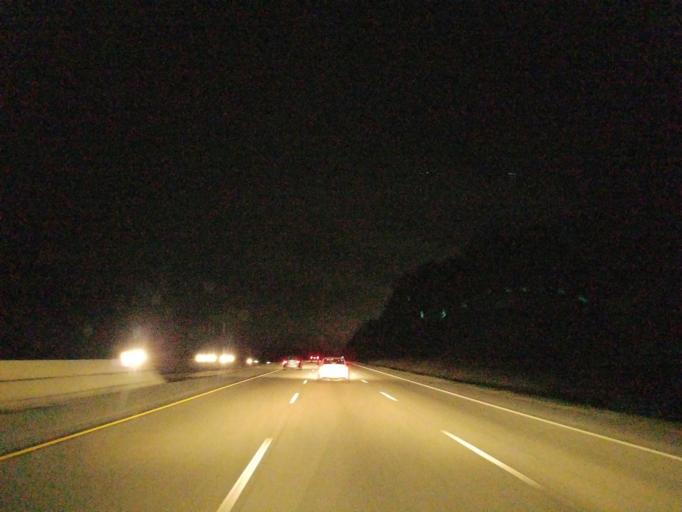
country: US
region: Alabama
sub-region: Tuscaloosa County
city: Coaling
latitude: 33.1870
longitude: -87.3330
